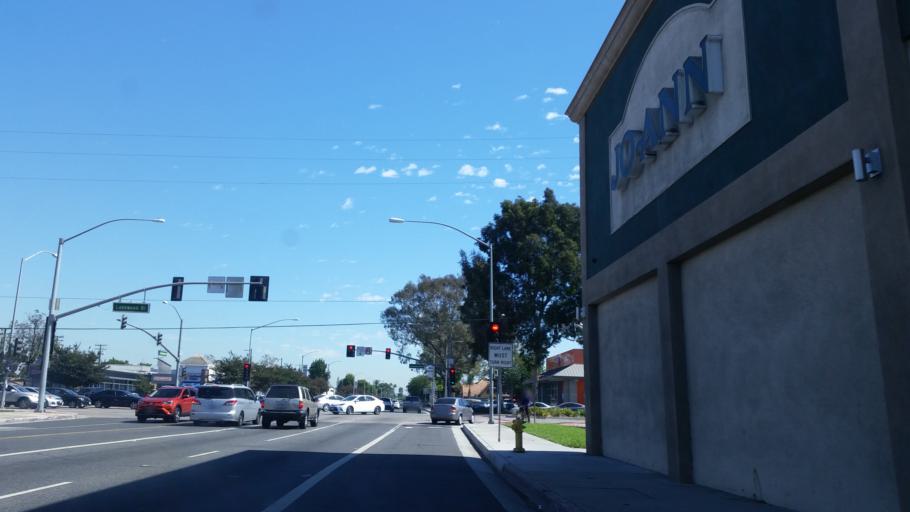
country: US
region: California
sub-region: Los Angeles County
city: Lakewood
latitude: 33.8537
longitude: -118.1433
